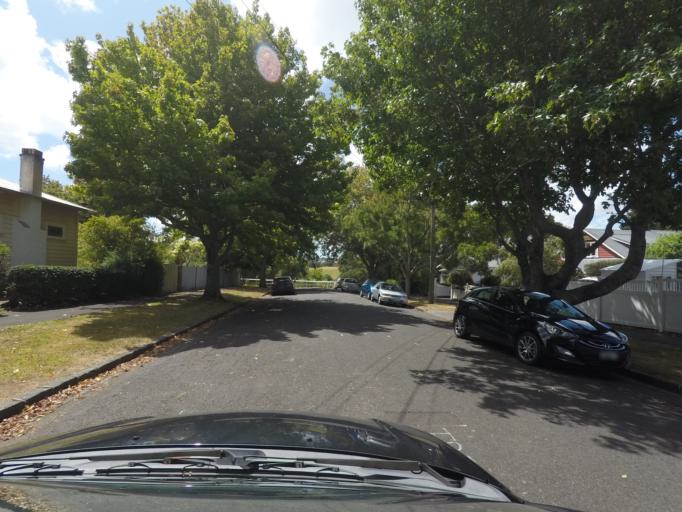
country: NZ
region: Auckland
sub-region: Auckland
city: Rosebank
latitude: -36.8565
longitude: 174.7078
